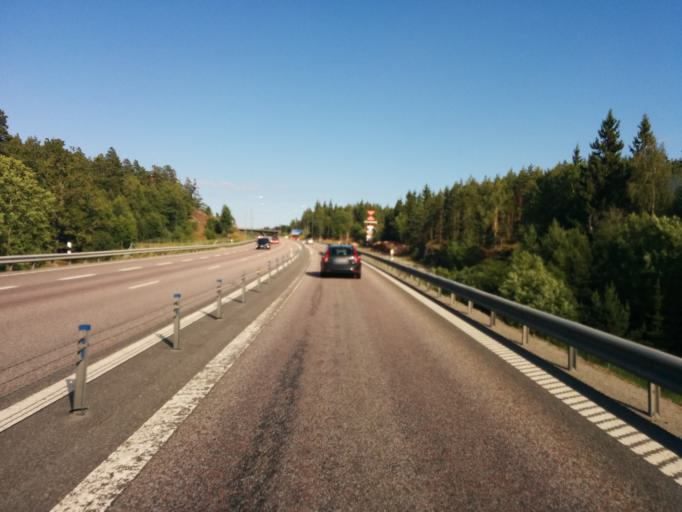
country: SE
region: Stockholm
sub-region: Varmdo Kommun
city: Gustavsberg
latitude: 59.3079
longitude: 18.3747
